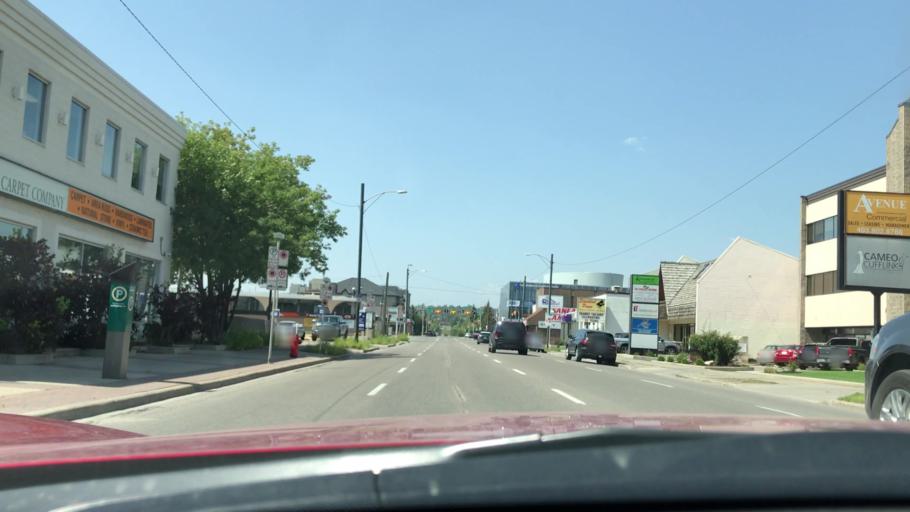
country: CA
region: Alberta
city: Calgary
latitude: 51.0432
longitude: -114.0922
